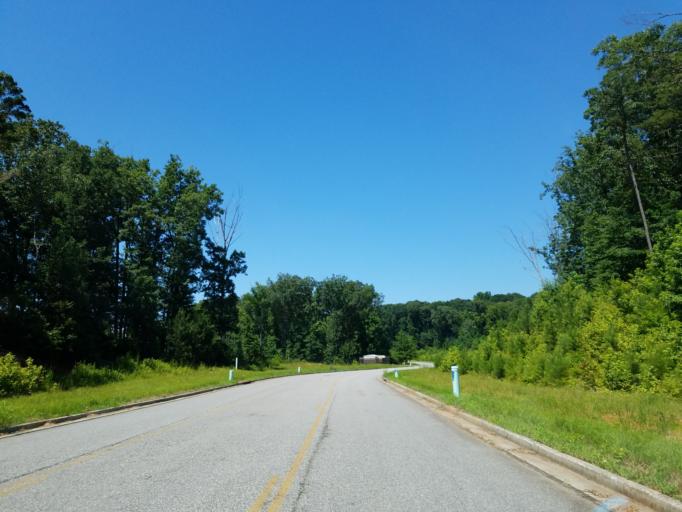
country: US
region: Georgia
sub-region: Forsyth County
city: Cumming
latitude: 34.2714
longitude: -84.0771
